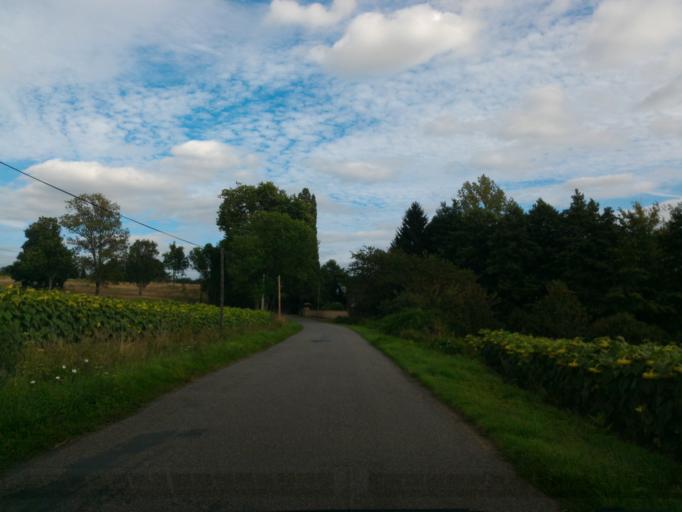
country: FR
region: Poitou-Charentes
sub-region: Departement de la Charente
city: Brigueuil
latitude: 45.9305
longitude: 0.8265
